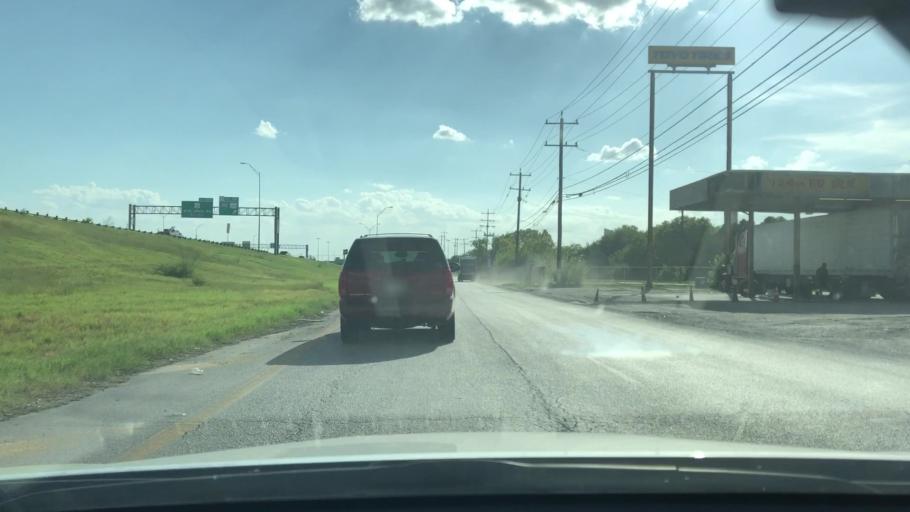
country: US
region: Texas
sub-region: Bexar County
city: Kirby
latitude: 29.4391
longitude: -98.3813
